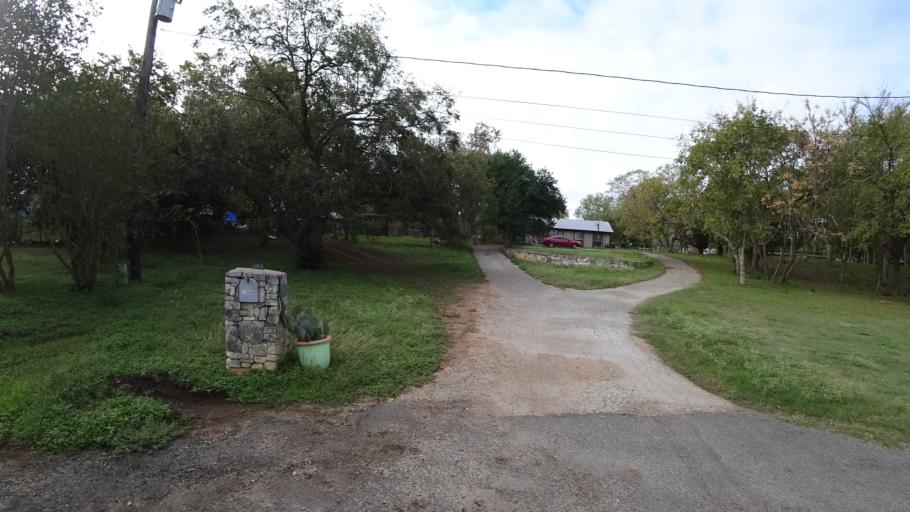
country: US
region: Texas
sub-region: Travis County
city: Manchaca
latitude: 30.1401
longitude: -97.8432
